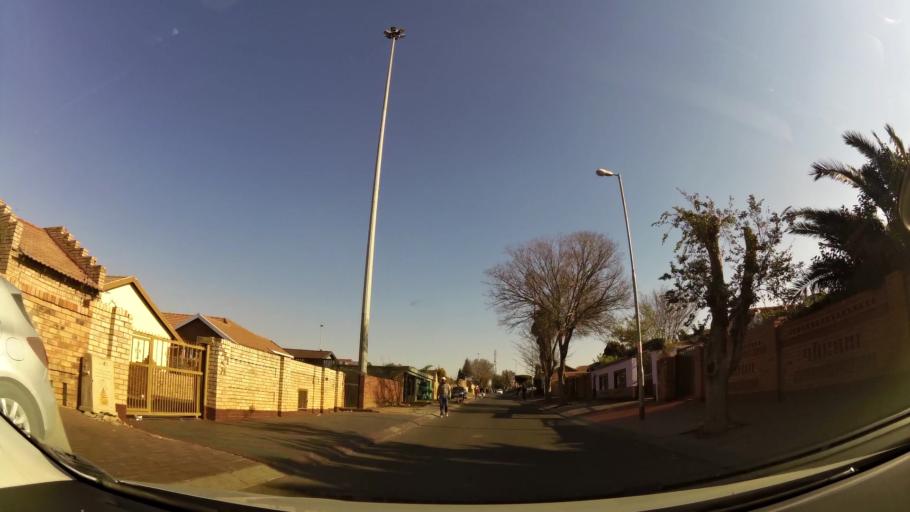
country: ZA
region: Gauteng
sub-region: City of Johannesburg Metropolitan Municipality
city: Soweto
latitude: -26.2660
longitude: 27.8788
